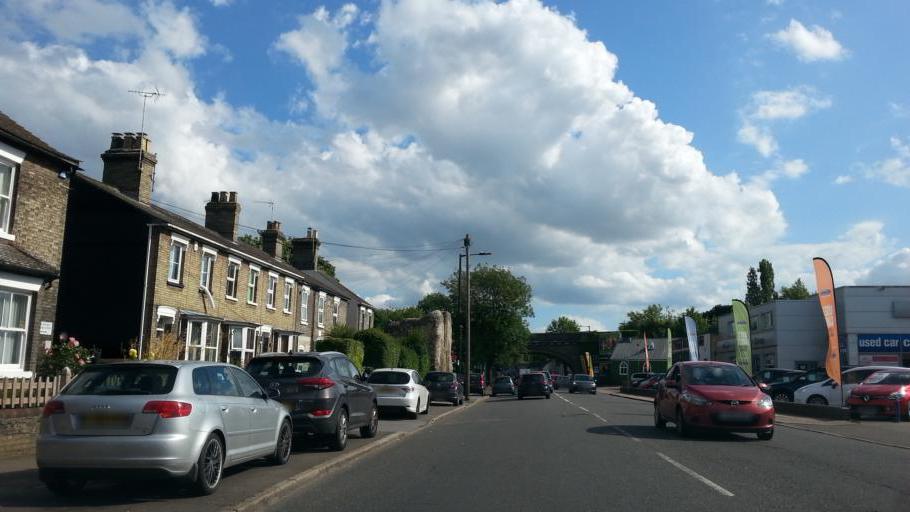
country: GB
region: England
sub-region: Suffolk
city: Bury St Edmunds
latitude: 52.2548
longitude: 0.7138
